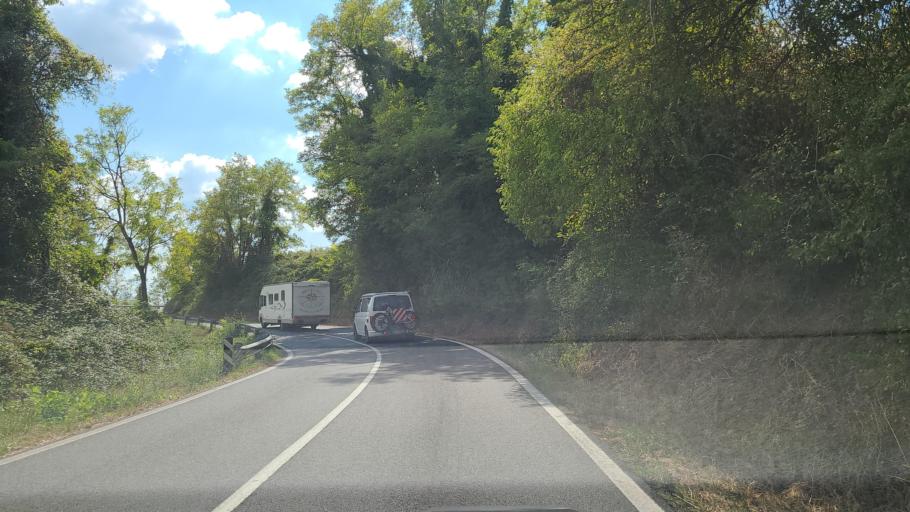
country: IT
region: Tuscany
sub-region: Provincia di Siena
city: San Gimignano
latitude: 43.4109
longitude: 11.0585
